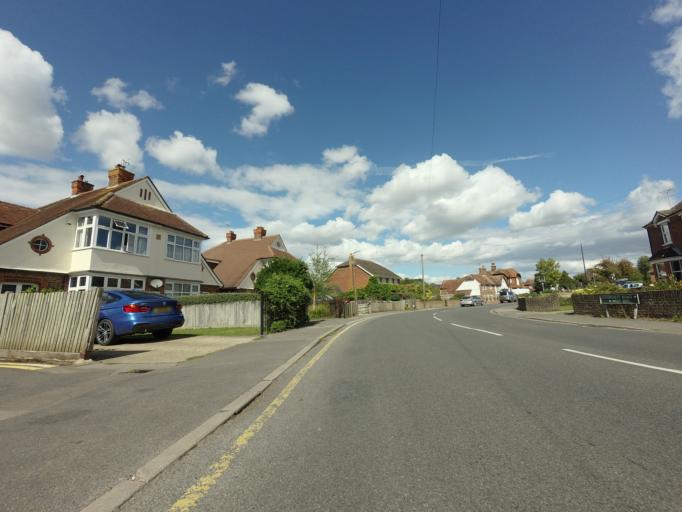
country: GB
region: England
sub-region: Kent
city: Marden
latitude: 51.1738
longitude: 0.4881
